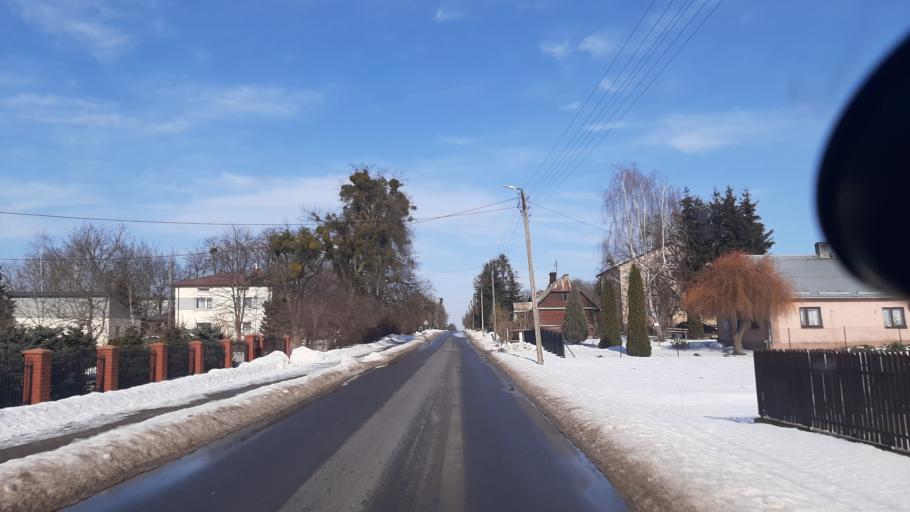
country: PL
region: Lublin Voivodeship
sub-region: Powiat pulawski
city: Wawolnica
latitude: 51.3330
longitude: 22.1095
